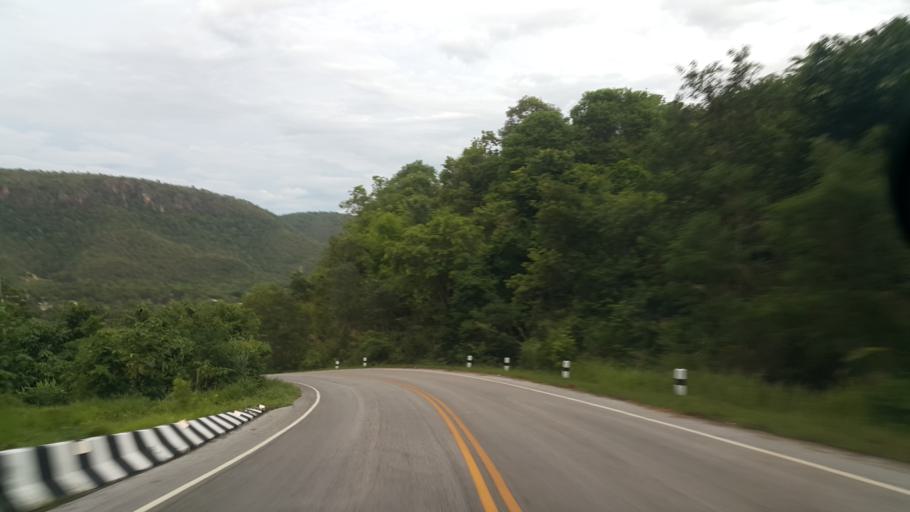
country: TH
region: Loei
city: Na Haeo
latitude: 17.4929
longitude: 101.1740
